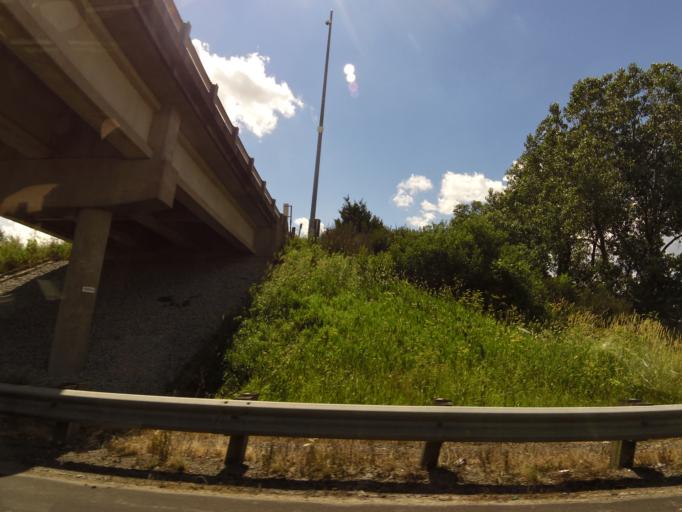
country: US
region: Iowa
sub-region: Johnson County
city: North Liberty
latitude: 41.7752
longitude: -91.6468
